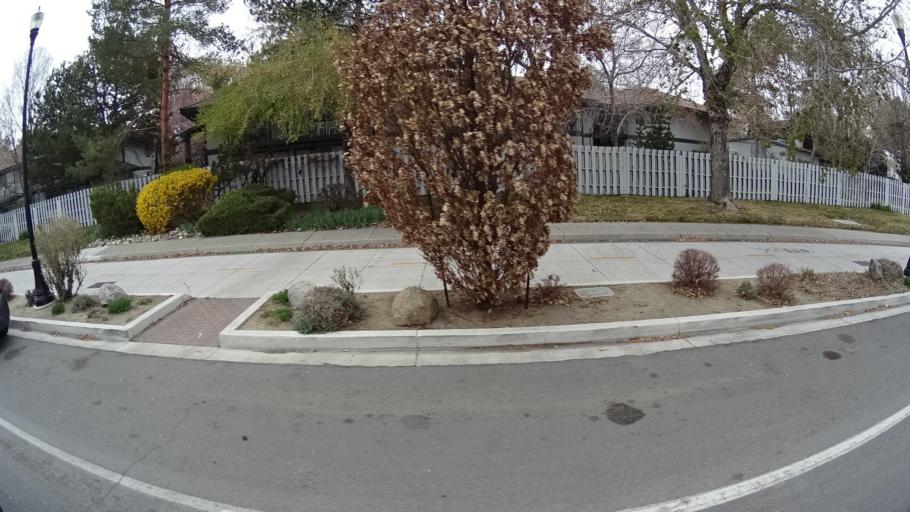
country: US
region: Nevada
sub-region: Washoe County
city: Sparks
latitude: 39.5364
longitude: -119.7406
